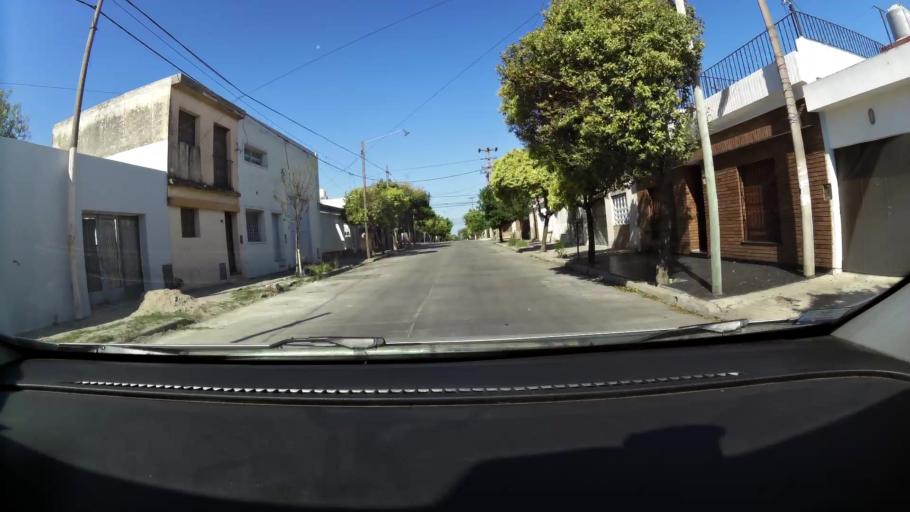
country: AR
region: Cordoba
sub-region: Departamento de Capital
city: Cordoba
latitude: -31.4060
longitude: -64.1538
